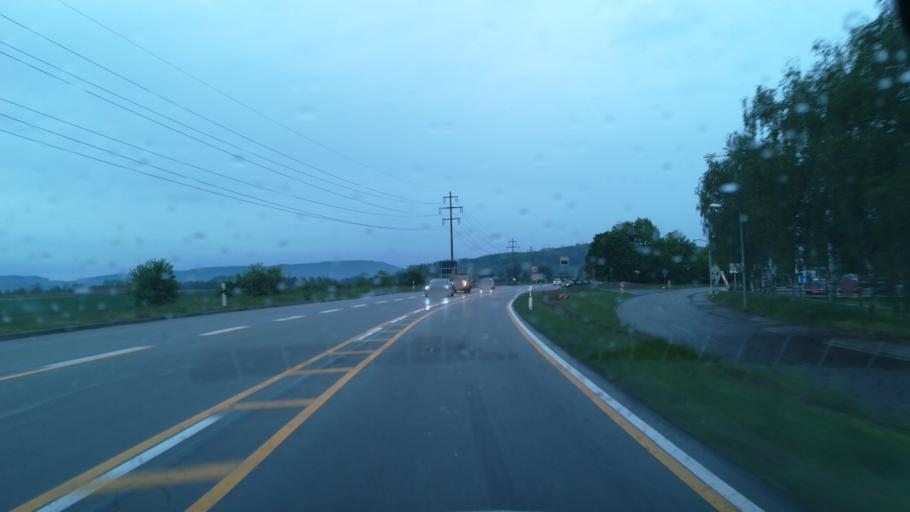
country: DE
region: Baden-Wuerttemberg
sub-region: Freiburg Region
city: Lottstetten
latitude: 47.6323
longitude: 8.5822
